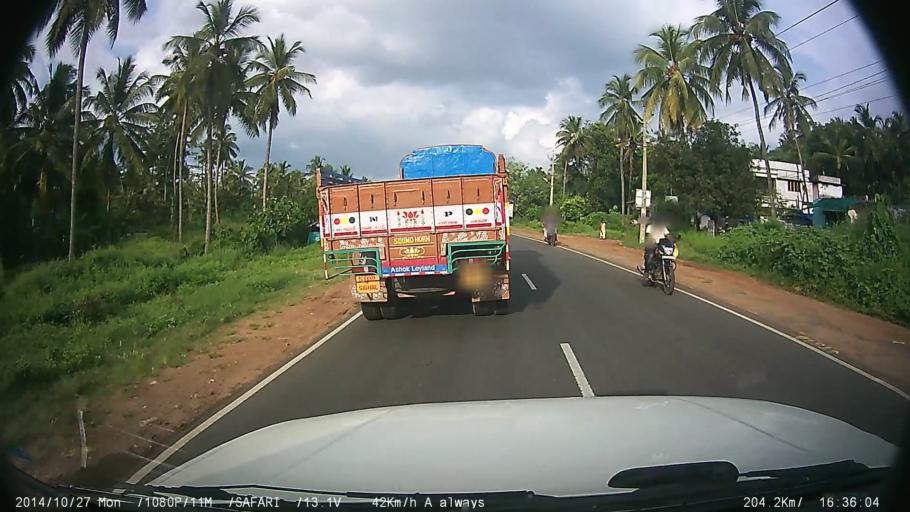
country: IN
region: Kerala
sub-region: Thrissur District
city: Trichur
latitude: 10.5403
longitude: 76.2849
